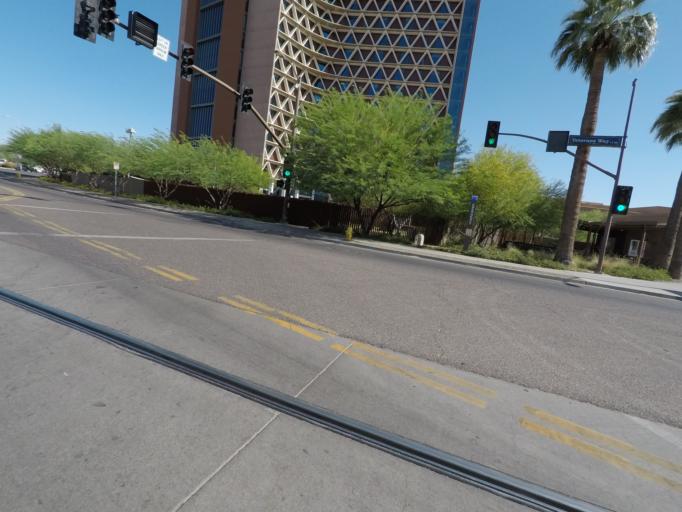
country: US
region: Arizona
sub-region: Maricopa County
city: Tempe Junction
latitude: 33.4233
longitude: -111.9305
